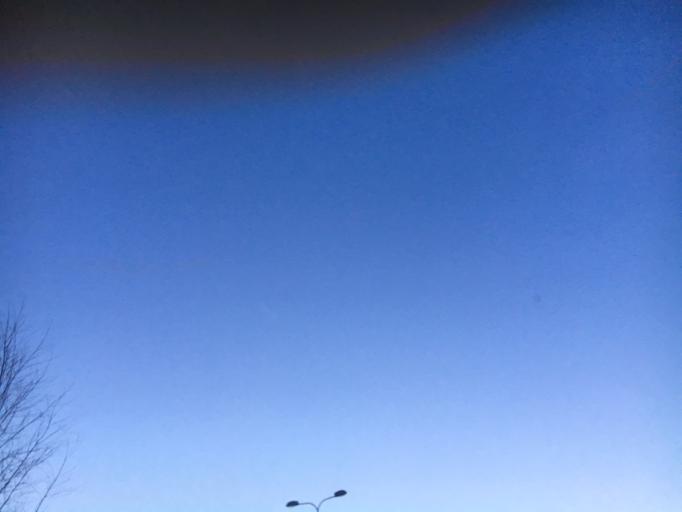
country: FI
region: Kainuu
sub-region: Kajaani
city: Kajaani
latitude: 64.2106
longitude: 27.7747
